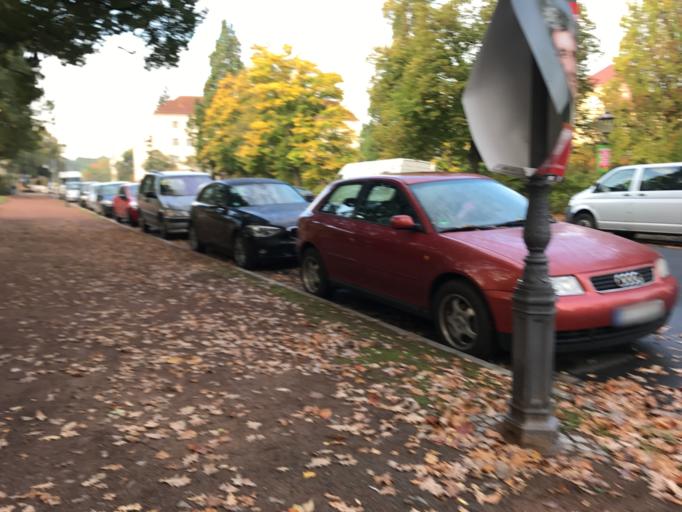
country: DE
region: Saxony
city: Dresden
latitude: 51.0435
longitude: 13.7743
